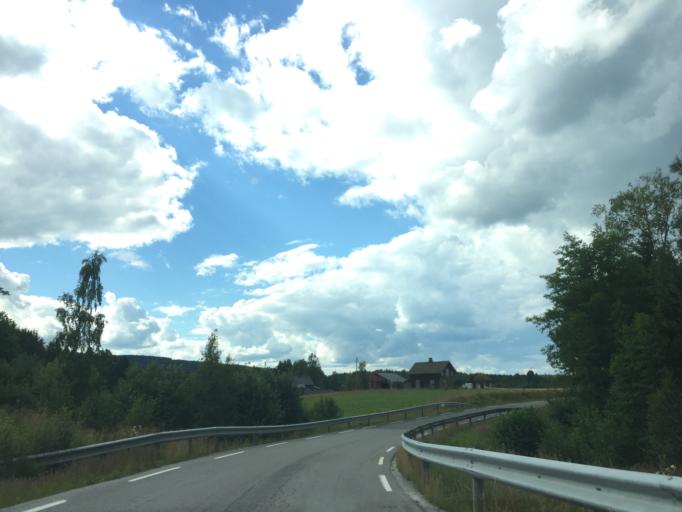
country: NO
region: Hedmark
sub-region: Kongsvinger
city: Spetalen
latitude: 60.1930
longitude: 11.8373
